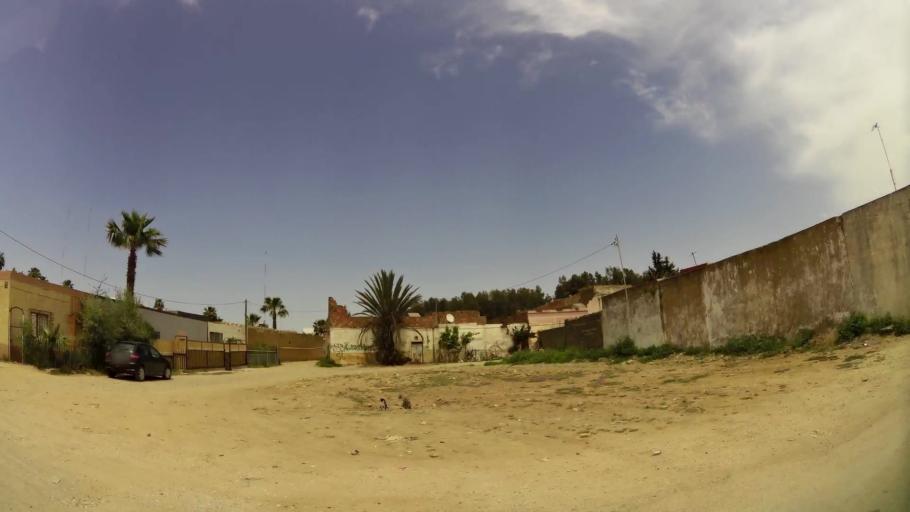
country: MA
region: Rabat-Sale-Zemmour-Zaer
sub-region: Khemisset
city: Khemisset
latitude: 33.8184
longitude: -6.0667
